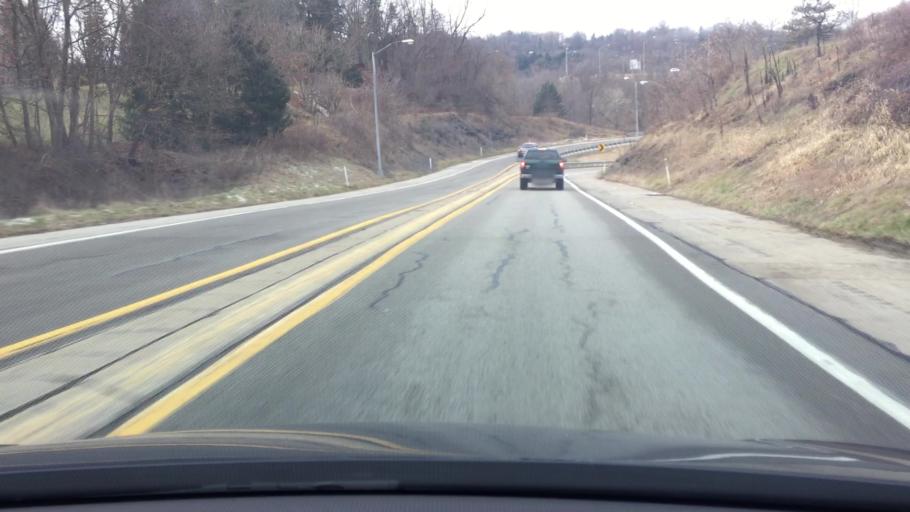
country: US
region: Pennsylvania
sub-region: Allegheny County
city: Churchill
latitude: 40.4410
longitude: -79.8259
